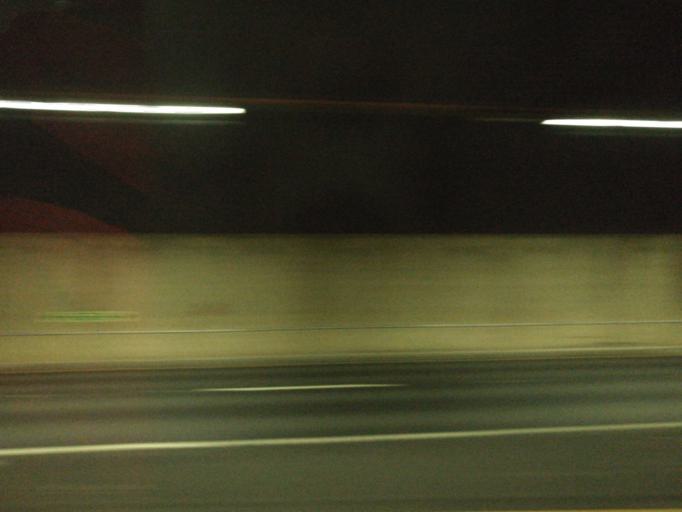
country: NO
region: Oslo
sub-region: Oslo
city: Oslo
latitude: 59.9026
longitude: 10.7669
